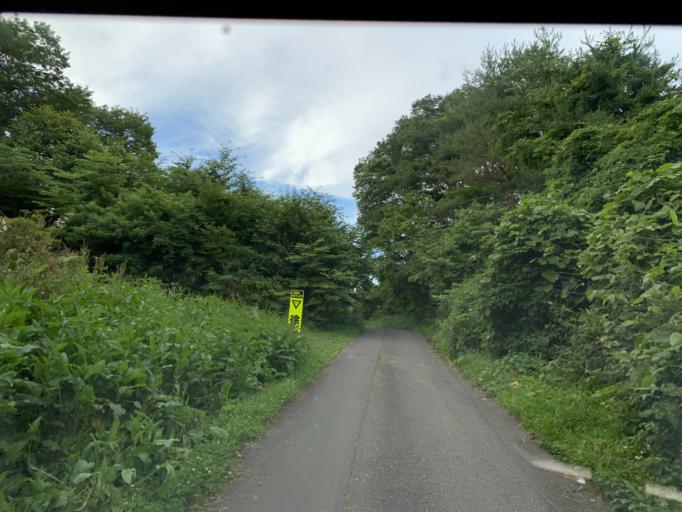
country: JP
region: Iwate
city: Ichinoseki
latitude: 38.9022
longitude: 141.0105
